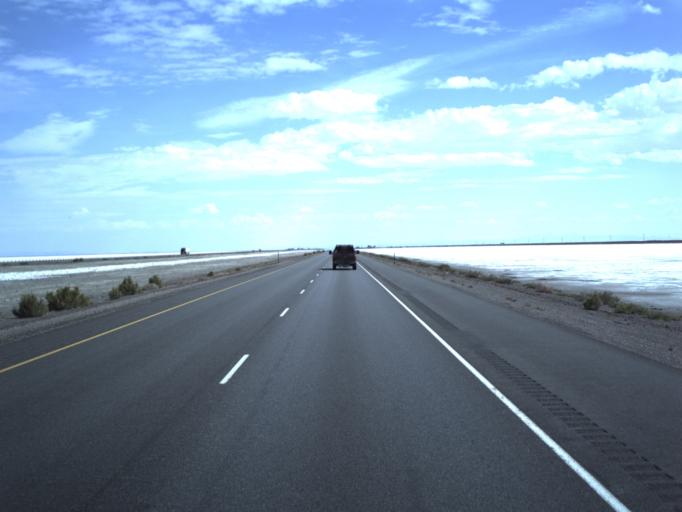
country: US
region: Utah
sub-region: Tooele County
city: Wendover
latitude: 40.7394
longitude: -113.8995
